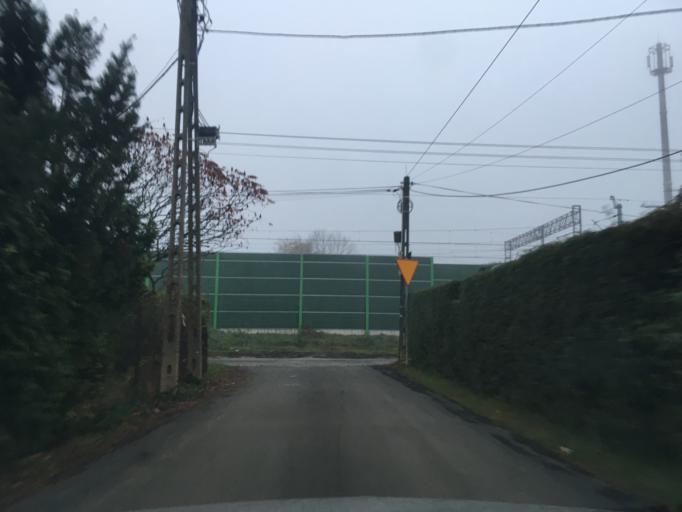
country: PL
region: Masovian Voivodeship
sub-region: Powiat pruszkowski
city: Brwinow
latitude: 52.1424
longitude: 20.7218
